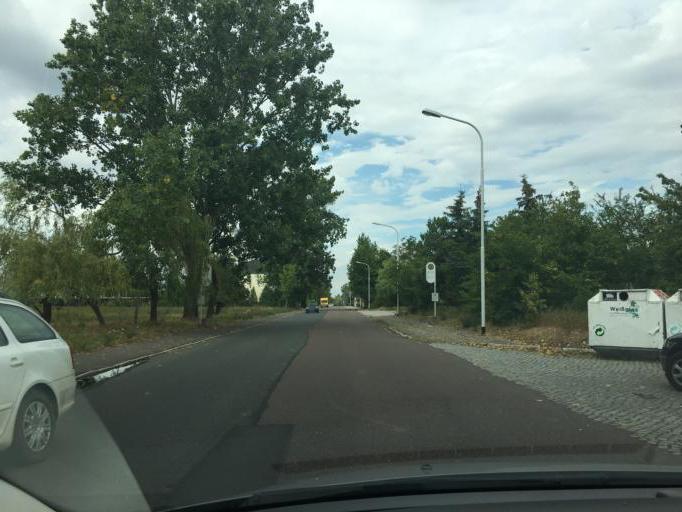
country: DE
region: Saxony-Anhalt
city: Angersdorf
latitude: 51.4443
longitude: 11.9447
